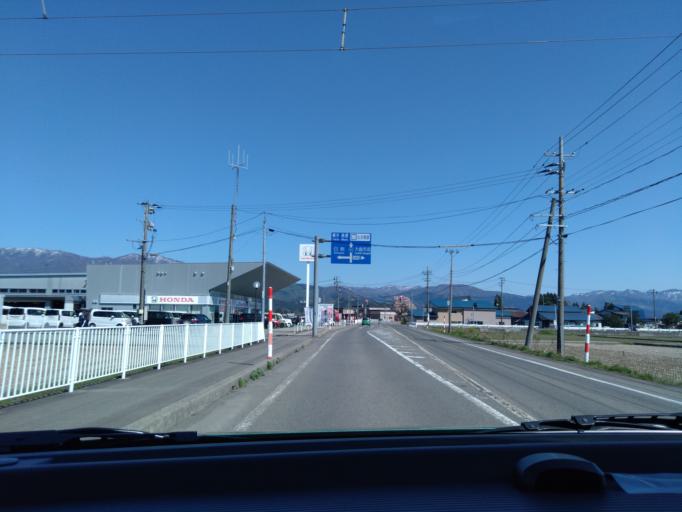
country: JP
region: Akita
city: Kakunodatemachi
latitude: 39.5720
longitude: 140.5785
